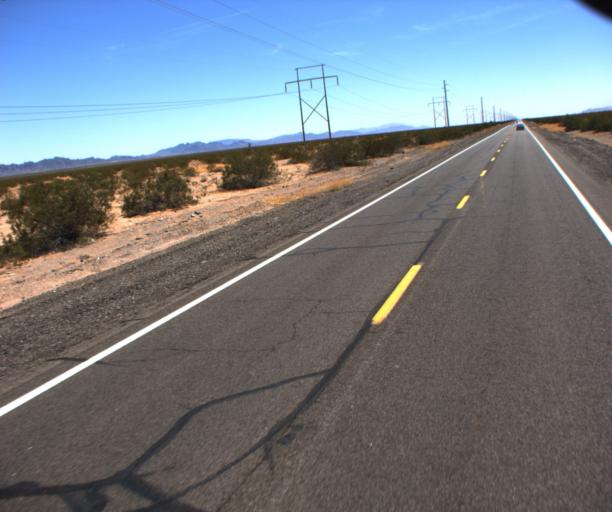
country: US
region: Arizona
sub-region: La Paz County
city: Parker
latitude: 33.9251
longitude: -114.2169
